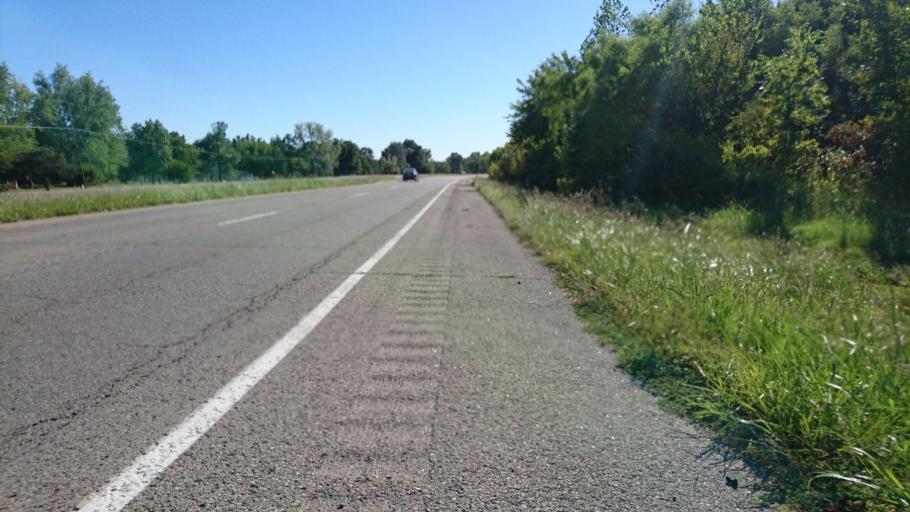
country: US
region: Oklahoma
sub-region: Rogers County
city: Justice
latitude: 36.3732
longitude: -95.5630
